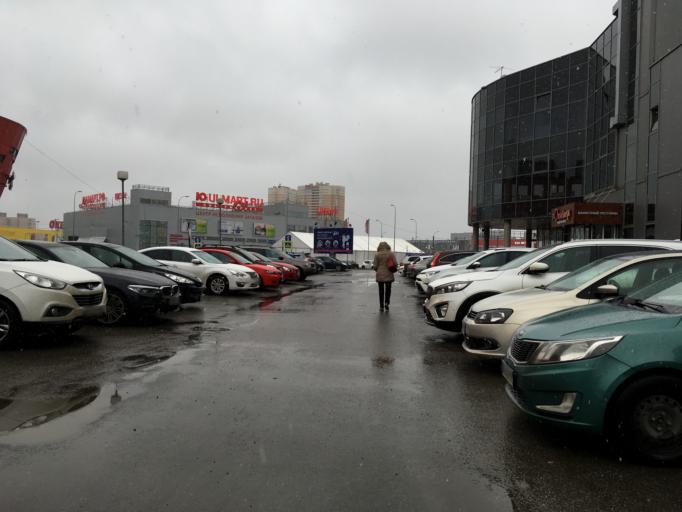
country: RU
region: St.-Petersburg
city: Komendantsky aerodrom
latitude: 60.0013
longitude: 30.2661
